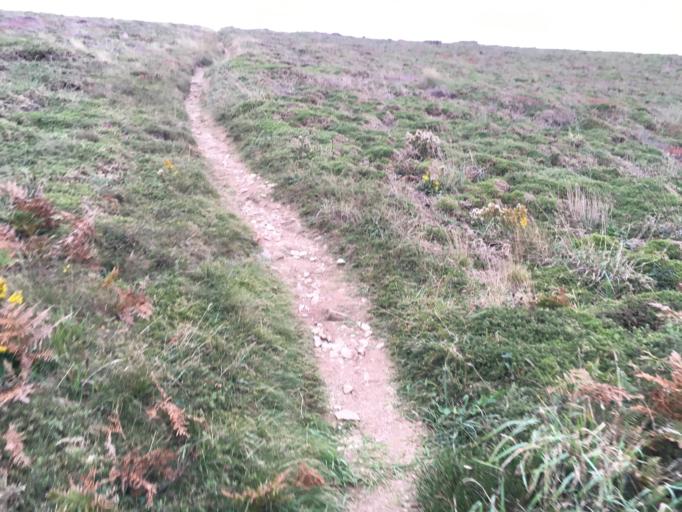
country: FR
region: Brittany
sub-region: Departement du Finistere
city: Plogoff
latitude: 48.0522
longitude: -4.7085
